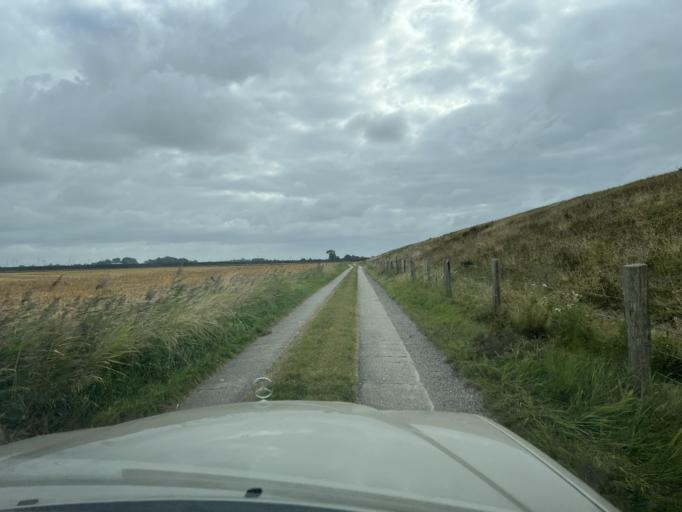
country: DE
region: Schleswig-Holstein
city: Lehe
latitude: 54.3300
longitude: 8.9925
